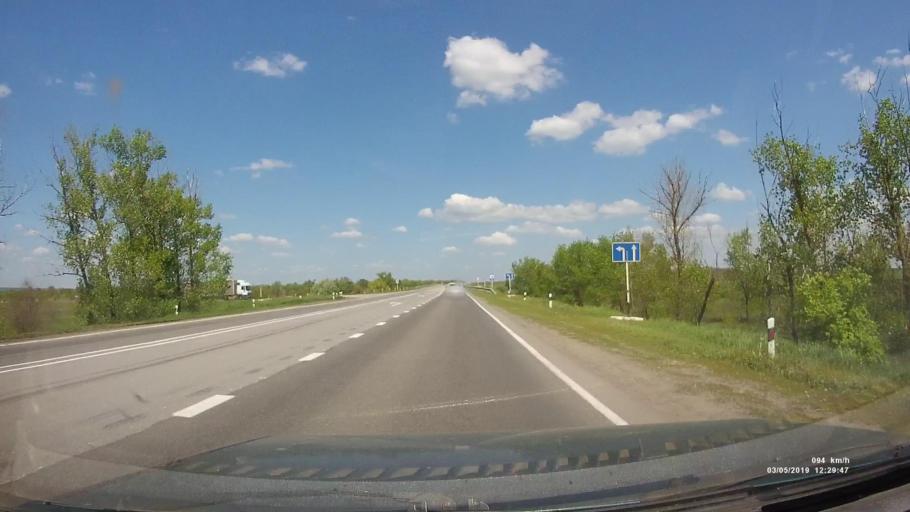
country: RU
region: Rostov
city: Semikarakorsk
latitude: 47.4924
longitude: 40.7382
